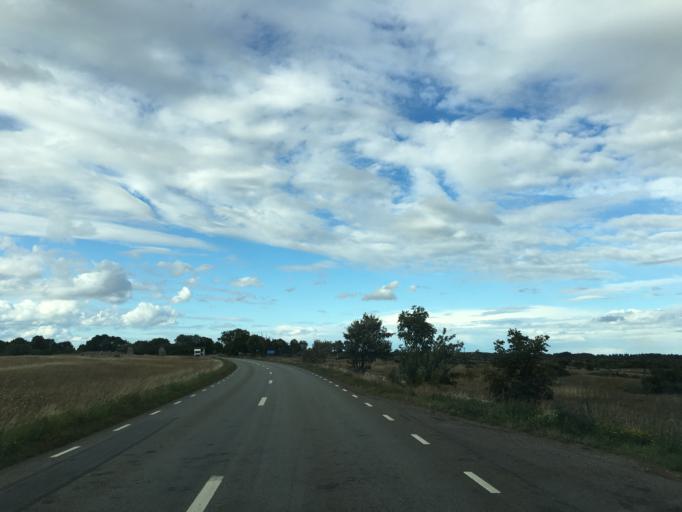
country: SE
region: Kalmar
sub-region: Morbylanga Kommun
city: Moerbylanga
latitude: 56.3863
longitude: 16.4343
